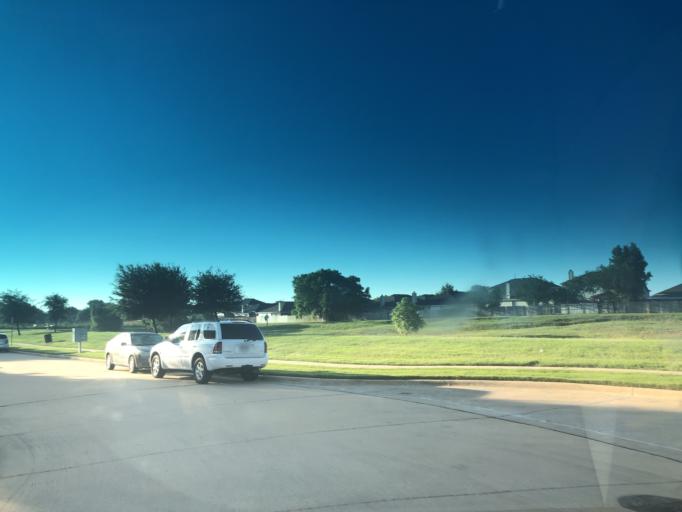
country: US
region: Texas
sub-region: Dallas County
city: Grand Prairie
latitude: 32.7025
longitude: -97.0184
